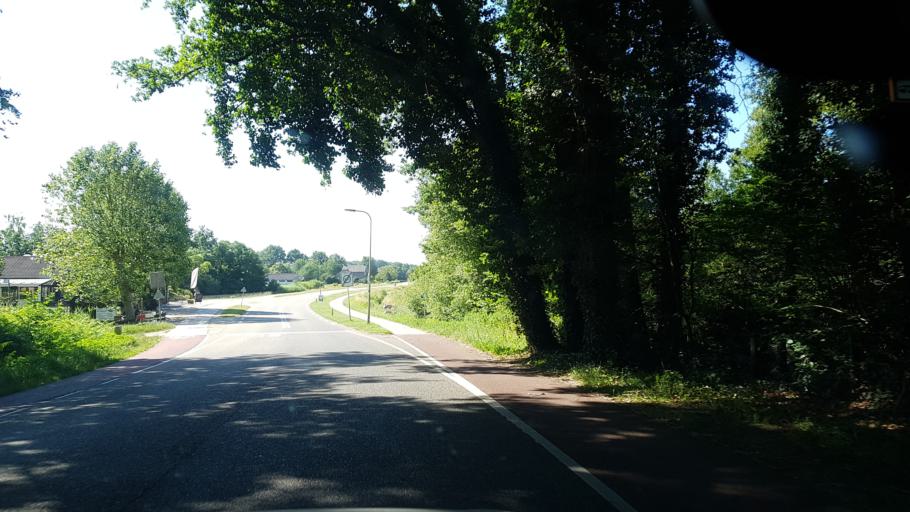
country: NL
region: Gelderland
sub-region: Gemeente Groesbeek
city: Bredeweg
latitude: 51.7384
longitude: 5.9551
